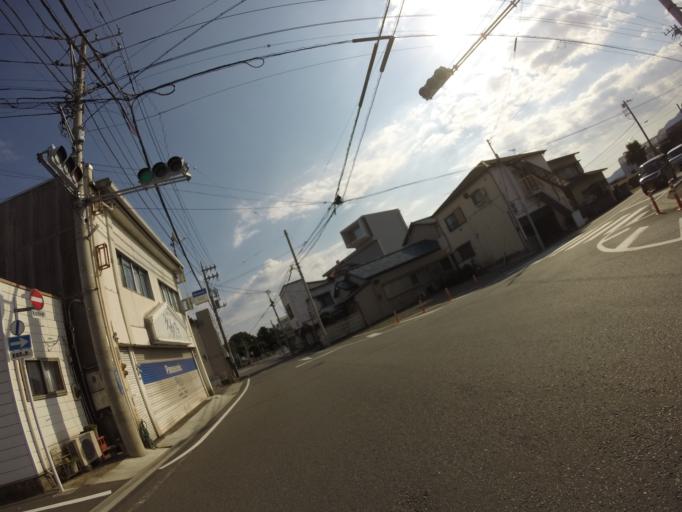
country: JP
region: Shizuoka
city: Fuji
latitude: 35.1855
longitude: 138.6467
